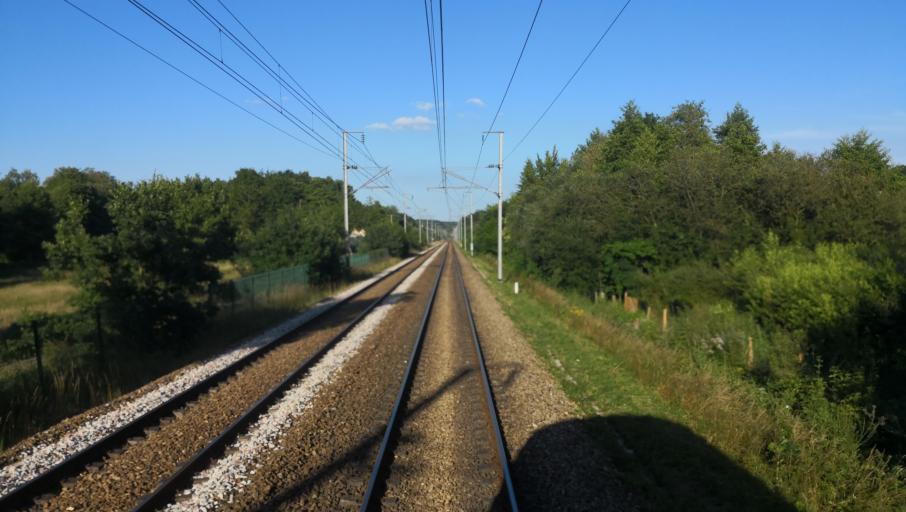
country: FR
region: Haute-Normandie
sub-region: Departement de l'Eure
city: Saint-Sebastien-de-Morsent
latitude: 48.9944
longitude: 1.0740
